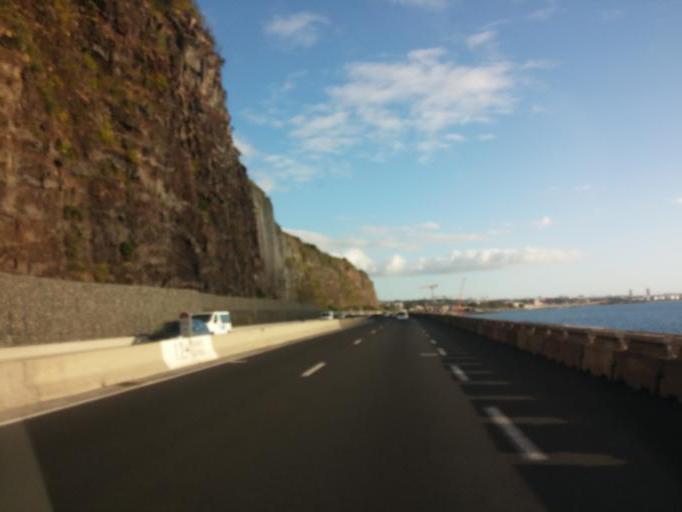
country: RE
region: Reunion
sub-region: Reunion
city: La Possession
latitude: -20.9142
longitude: 55.3508
